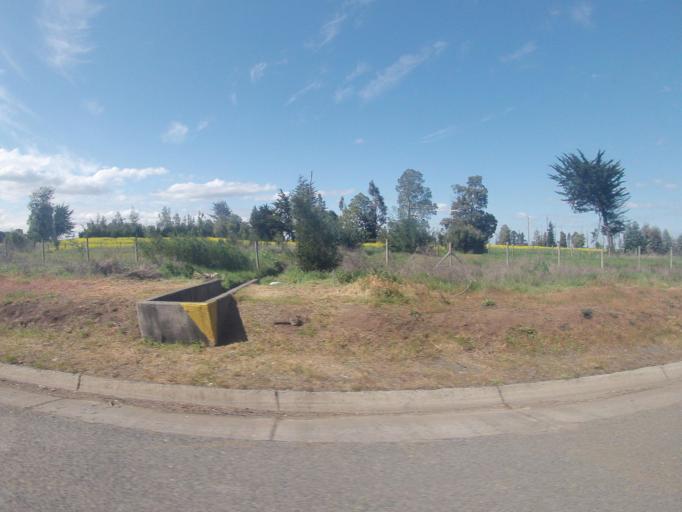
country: CL
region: Biobio
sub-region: Provincia de Biobio
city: Los Angeles
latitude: -37.4474
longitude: -72.4051
